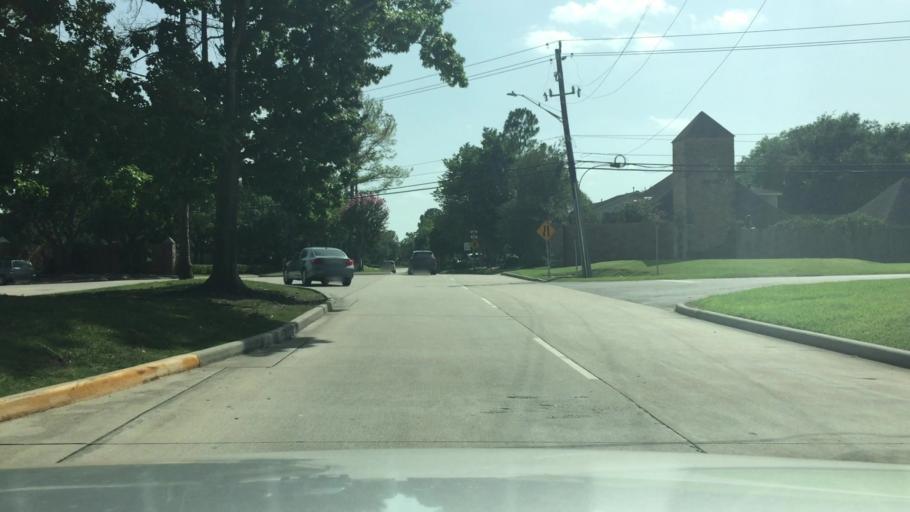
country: US
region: Texas
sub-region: Harris County
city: Bunker Hill Village
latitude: 29.7555
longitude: -95.5761
